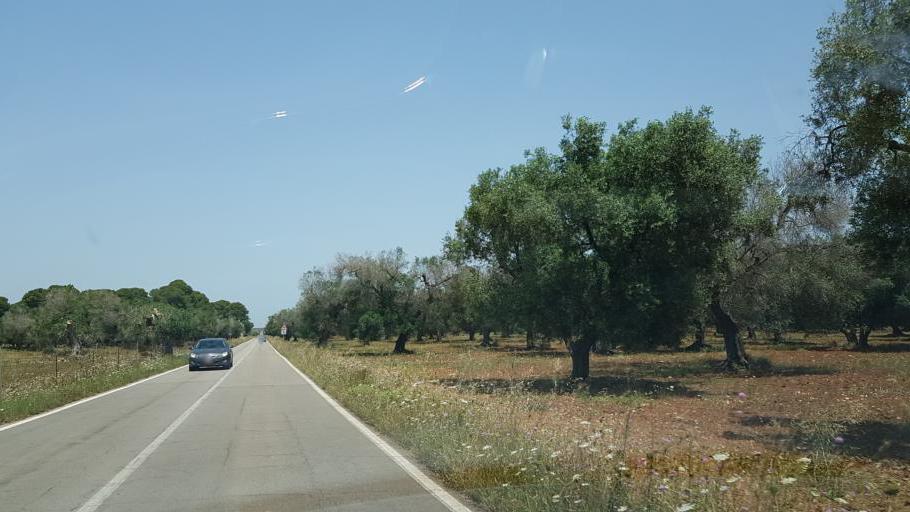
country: IT
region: Apulia
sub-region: Provincia di Lecce
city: Porto Cesareo
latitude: 40.3055
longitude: 17.9186
